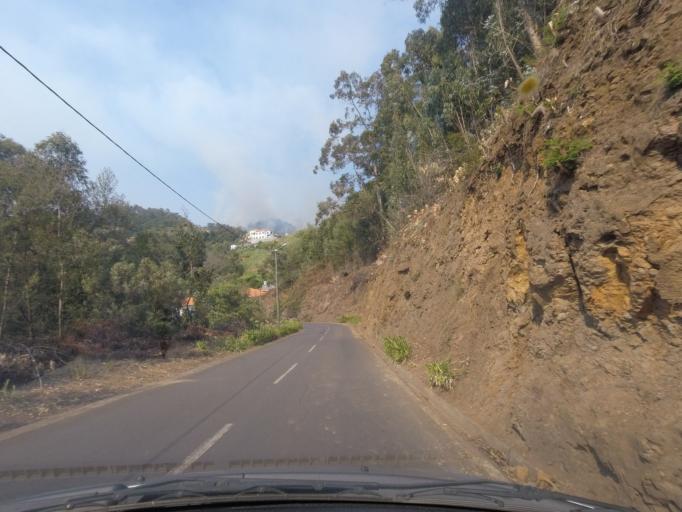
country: PT
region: Madeira
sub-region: Ribeira Brava
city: Campanario
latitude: 32.6899
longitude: -17.0579
